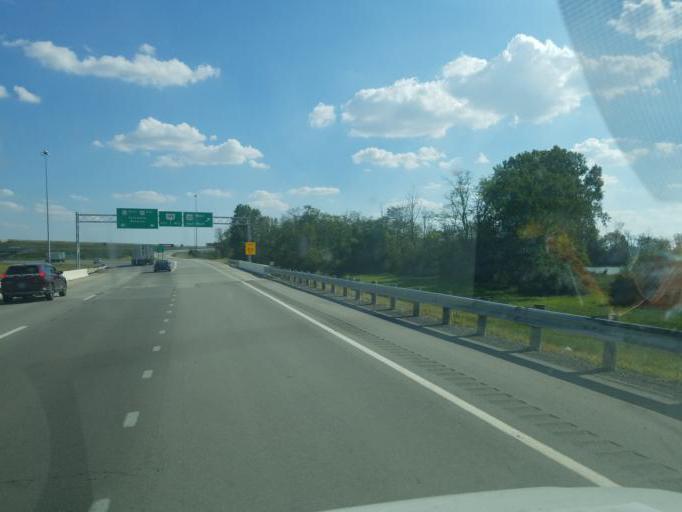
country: US
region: Ohio
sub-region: Wyandot County
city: Upper Sandusky
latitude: 40.8595
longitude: -83.3217
